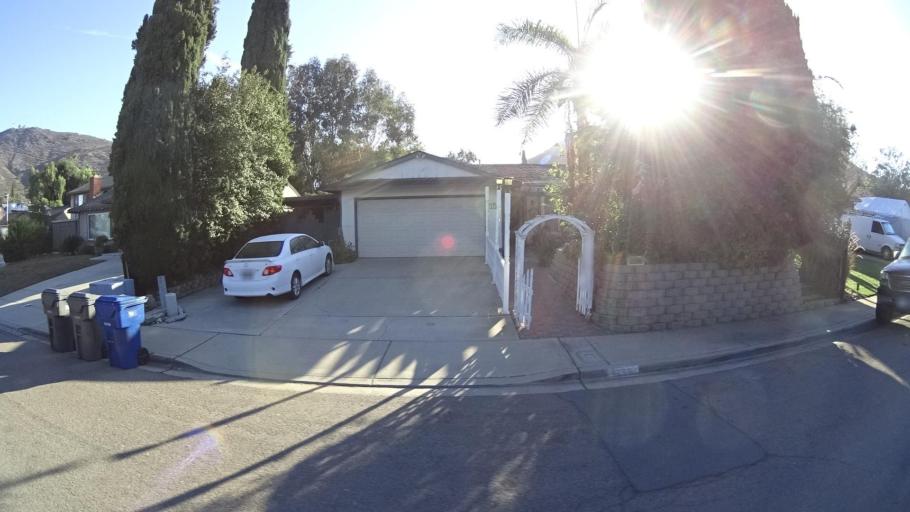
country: US
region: California
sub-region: San Diego County
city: Bostonia
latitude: 32.8205
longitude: -116.9460
